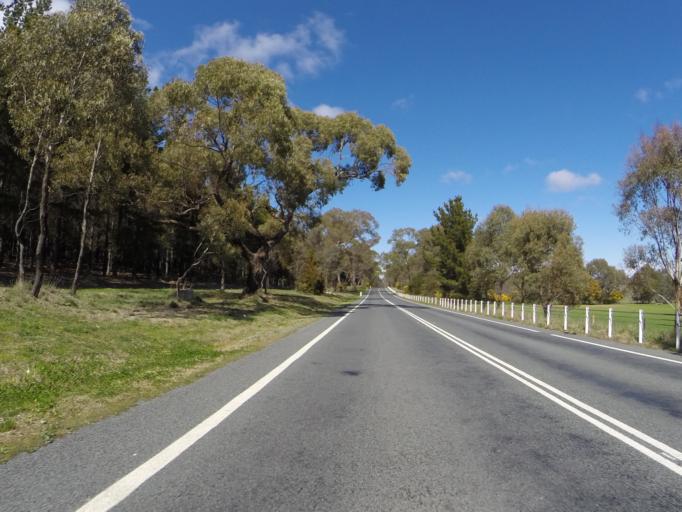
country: AU
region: New South Wales
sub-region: Queanbeyan
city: Queanbeyan
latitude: -35.2942
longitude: 149.2555
